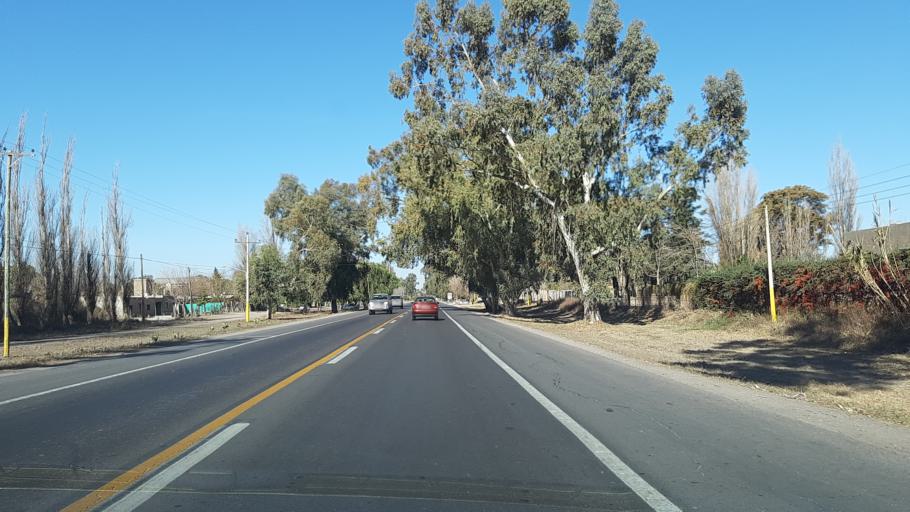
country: AR
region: San Juan
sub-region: Departamento de Santa Lucia
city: Santa Lucia
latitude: -31.5650
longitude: -68.4503
